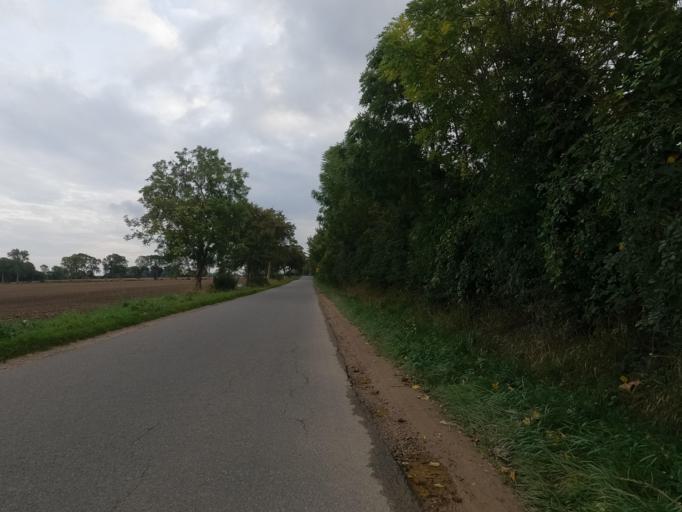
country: DE
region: Schleswig-Holstein
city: Neukirchen
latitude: 54.3222
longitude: 11.0348
